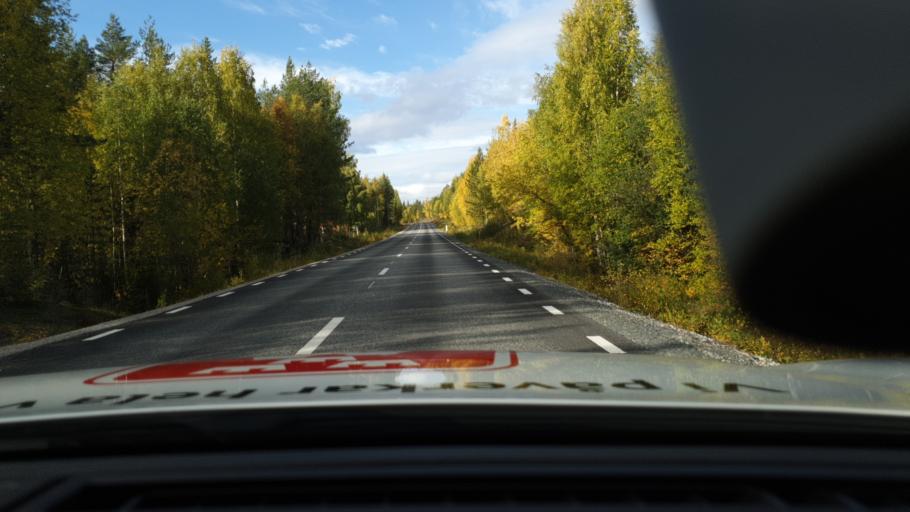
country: SE
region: Vaesterbotten
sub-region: Mala Kommun
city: Mala
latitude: 64.9780
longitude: 18.5637
